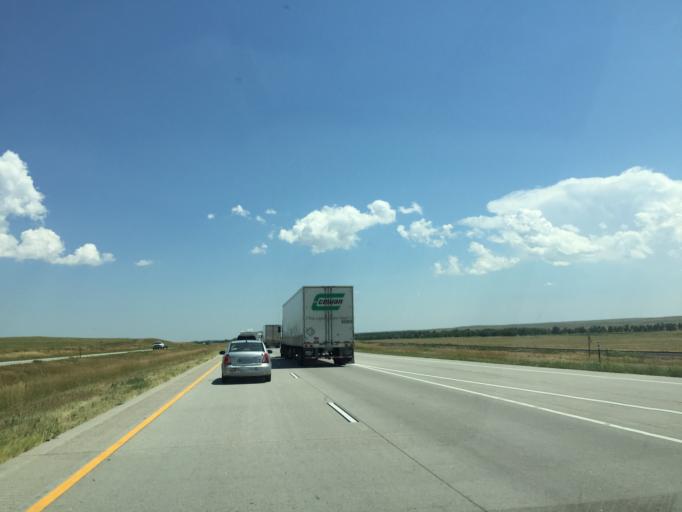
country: US
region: Colorado
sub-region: Lincoln County
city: Limon
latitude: 39.2904
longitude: -103.7940
